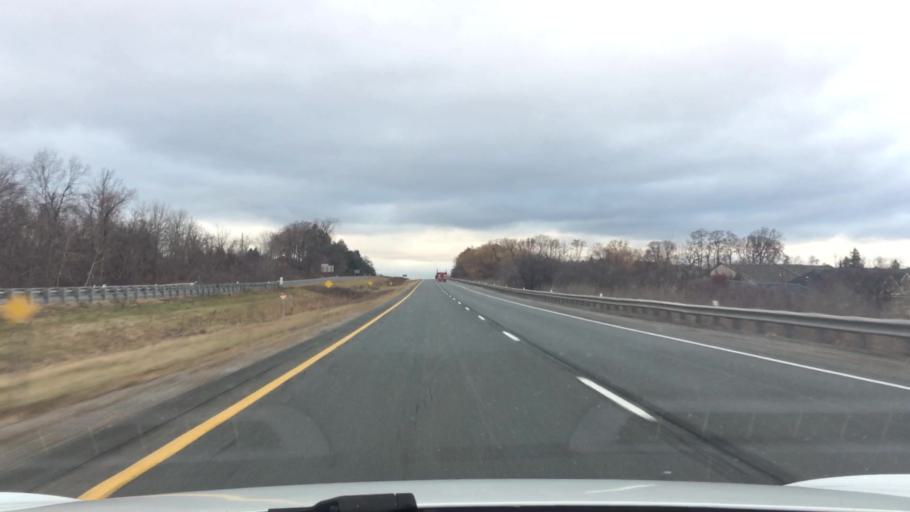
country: CA
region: Ontario
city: Niagara Falls
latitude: 43.1477
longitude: -79.1049
